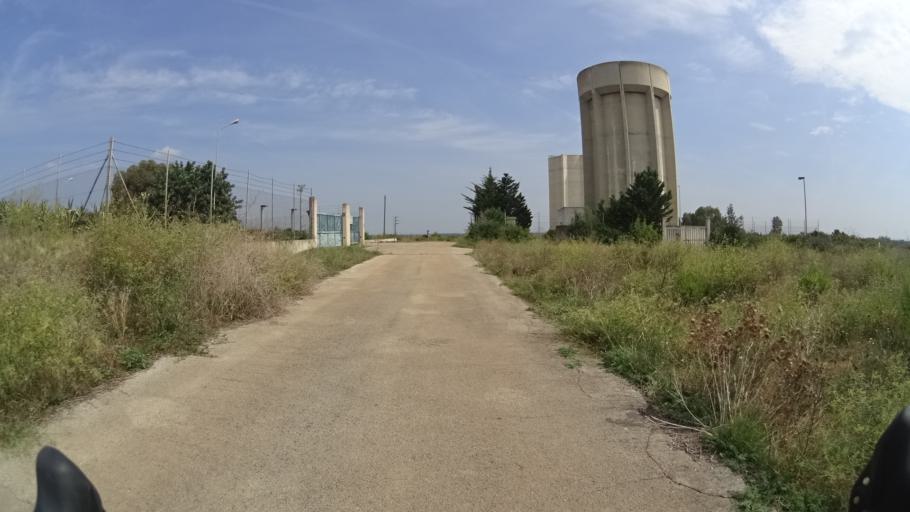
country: IT
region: Apulia
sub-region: Provincia di Brindisi
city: San Pancrazio Salentino
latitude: 40.3463
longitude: 17.8279
